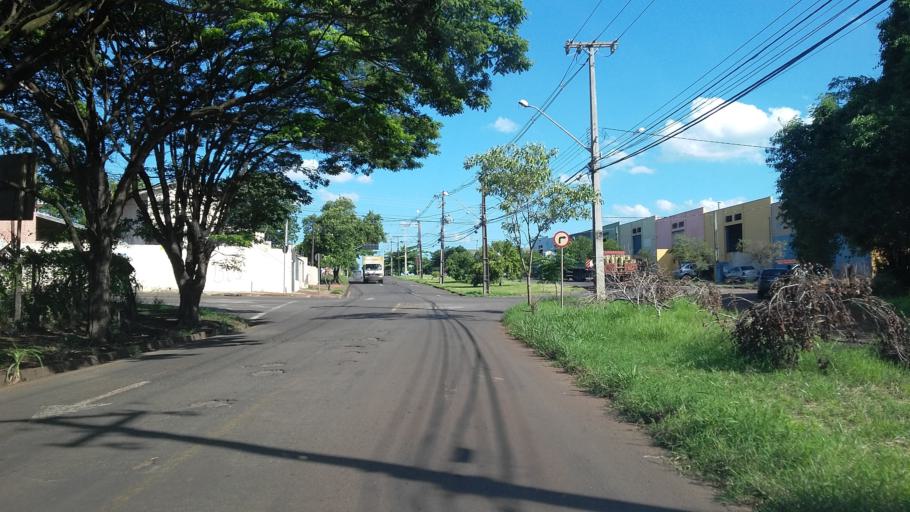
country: BR
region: Parana
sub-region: Londrina
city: Londrina
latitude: -23.2901
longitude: -51.2083
